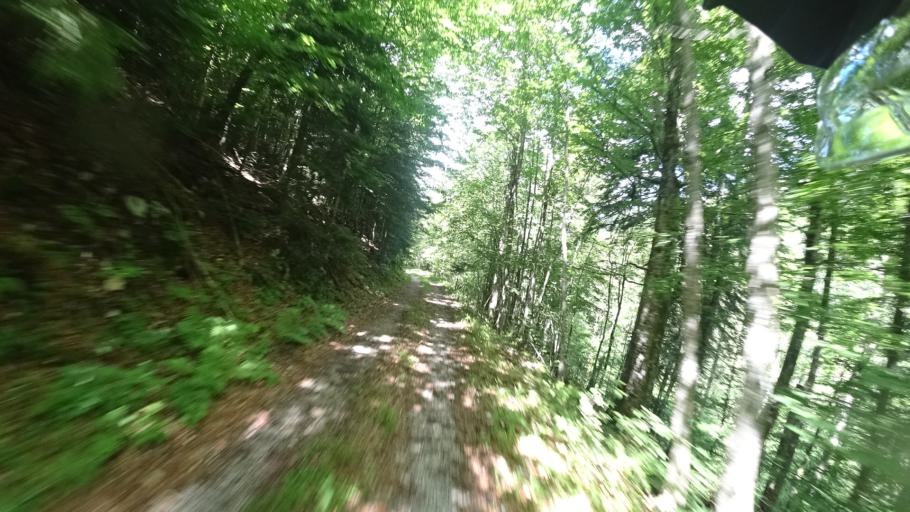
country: SI
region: Osilnica
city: Osilnica
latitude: 45.4964
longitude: 14.7148
